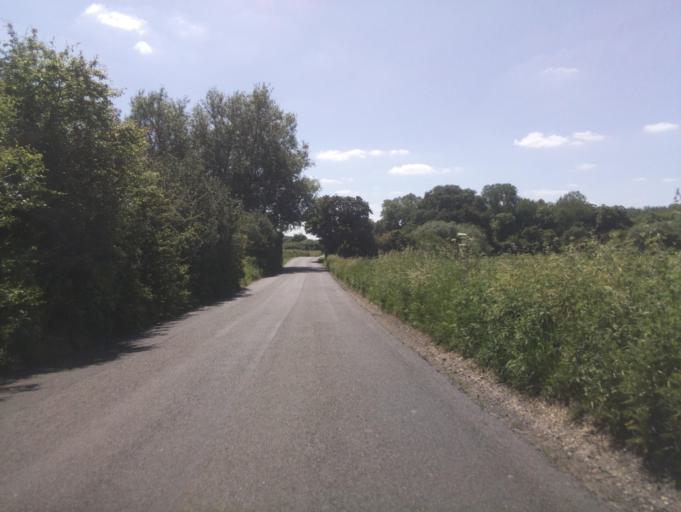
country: GB
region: England
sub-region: Wiltshire
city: Lyneham
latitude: 51.4746
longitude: -1.9556
